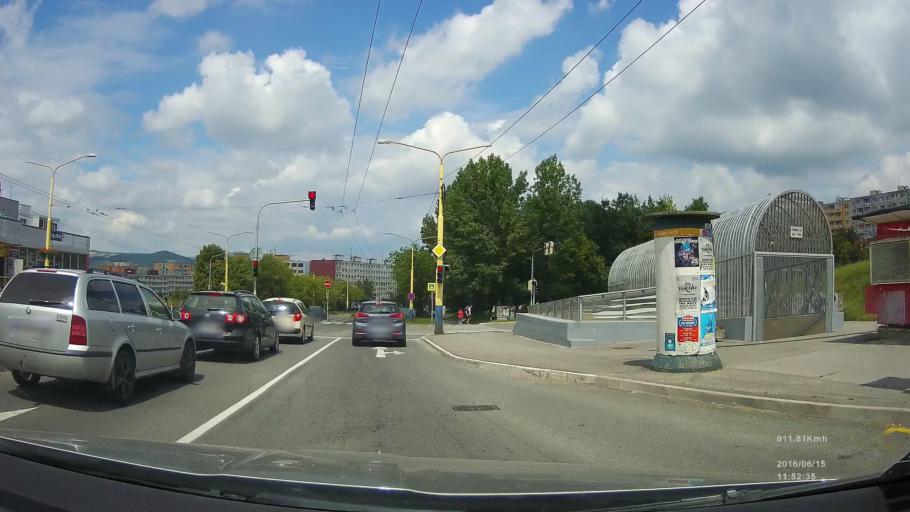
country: SK
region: Kosicky
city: Kosice
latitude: 48.7382
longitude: 21.2823
